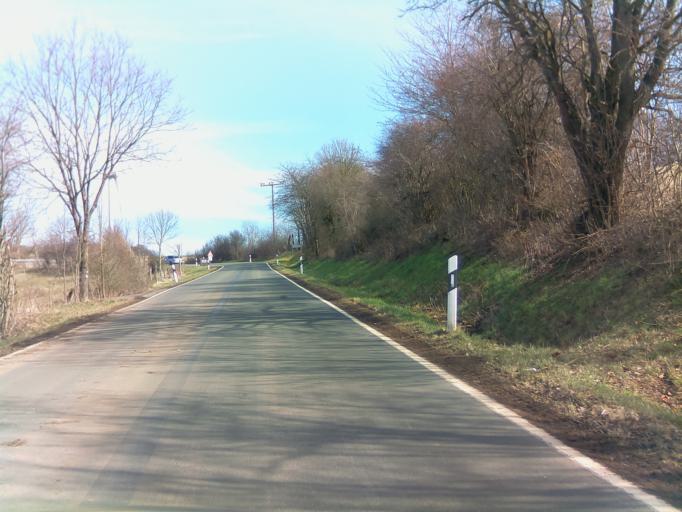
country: DE
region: Hesse
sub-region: Regierungsbezirk Giessen
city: Ulrichstein
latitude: 50.6198
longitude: 9.1226
